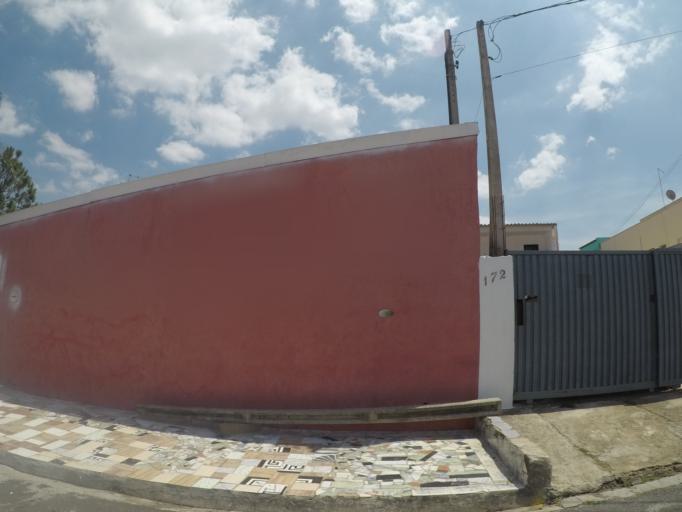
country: BR
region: Sao Paulo
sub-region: Cabreuva
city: Cabreuva
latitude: -23.2614
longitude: -47.0473
